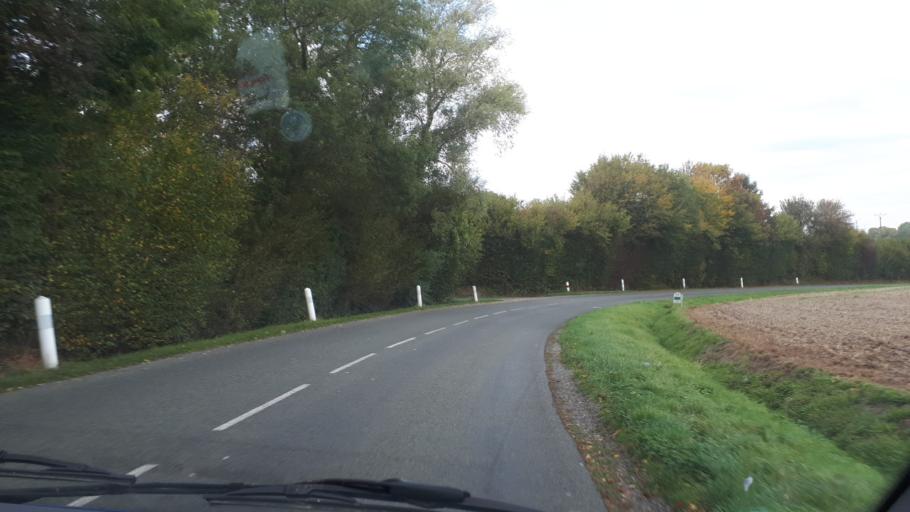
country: FR
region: Centre
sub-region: Departement d'Eure-et-Loir
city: Authon-du-Perche
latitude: 48.2261
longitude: 0.8735
